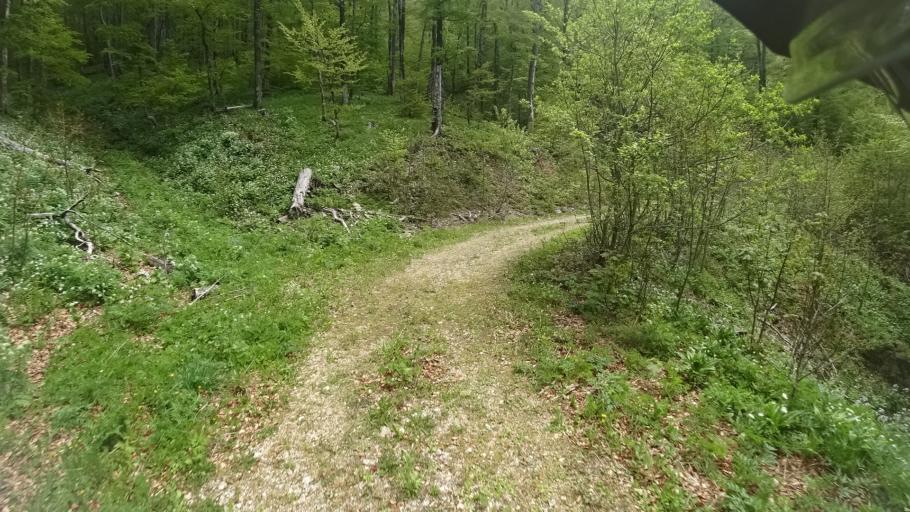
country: BA
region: Federation of Bosnia and Herzegovina
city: Orasac
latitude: 44.5771
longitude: 15.8730
